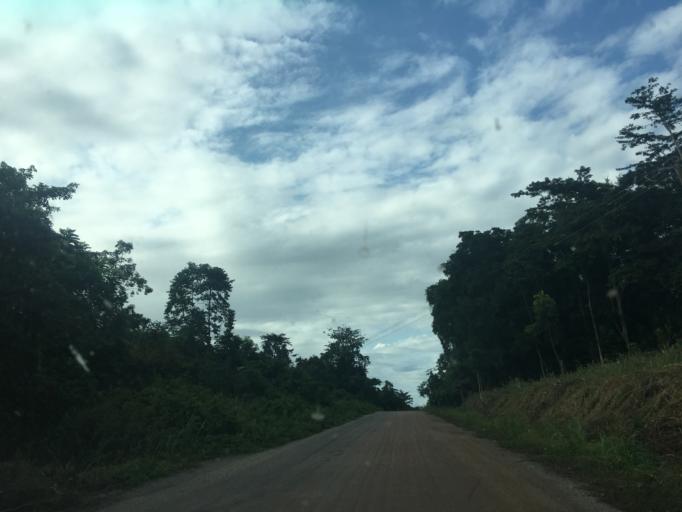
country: GH
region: Western
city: Wassa-Akropong
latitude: 5.9909
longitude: -2.4115
